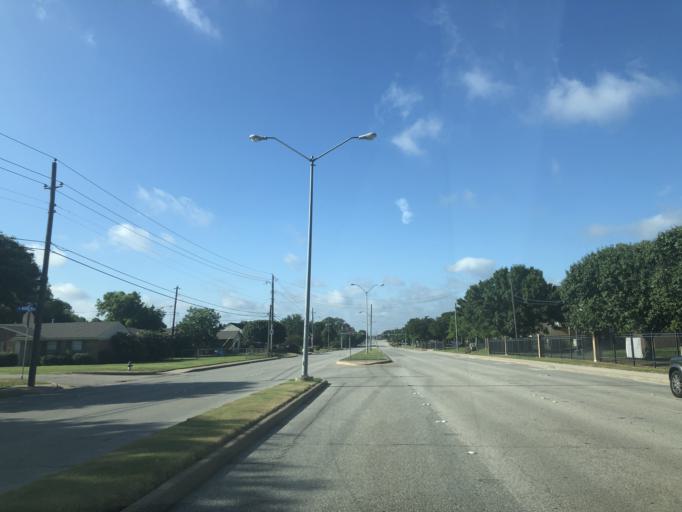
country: US
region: Texas
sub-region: Dallas County
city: Duncanville
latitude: 32.6611
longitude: -96.9258
